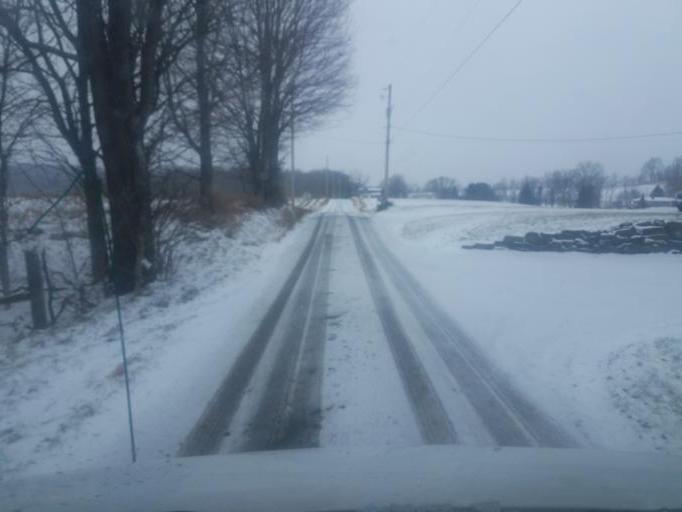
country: US
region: Ohio
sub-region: Sandusky County
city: Bellville
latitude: 40.6077
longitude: -82.4146
